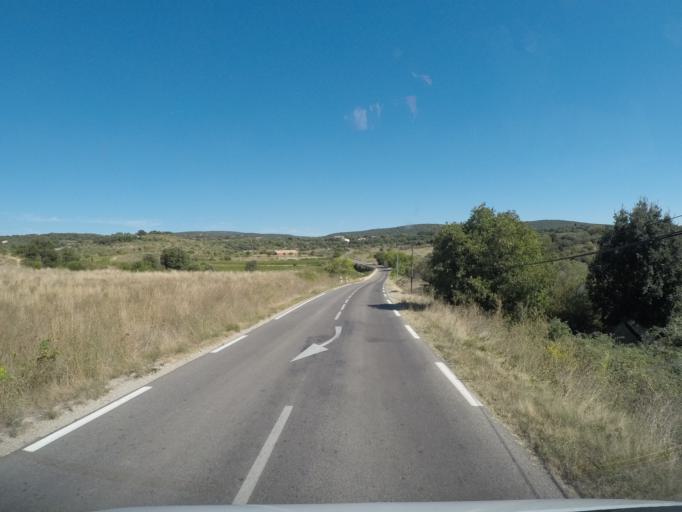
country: FR
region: Languedoc-Roussillon
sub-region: Departement de l'Herault
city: Aniane
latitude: 43.7107
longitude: 3.6064
